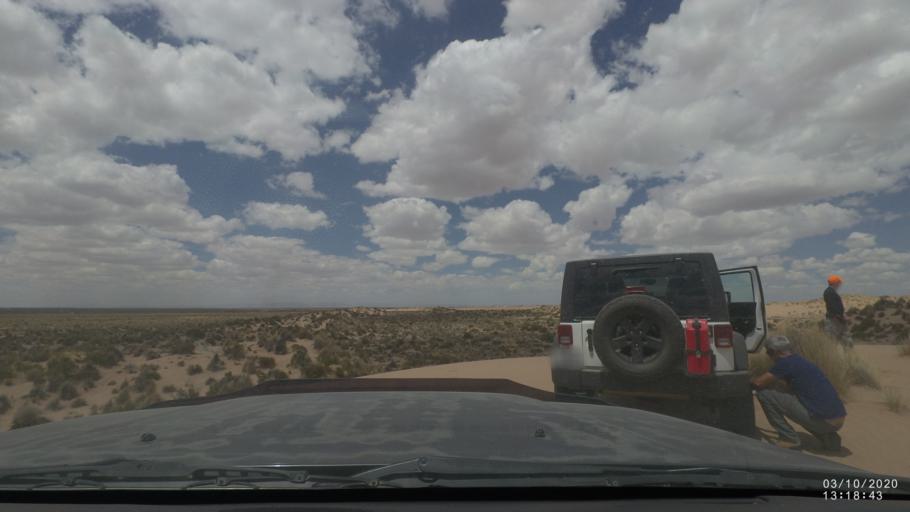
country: BO
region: Oruro
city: Poopo
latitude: -18.6909
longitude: -67.5324
